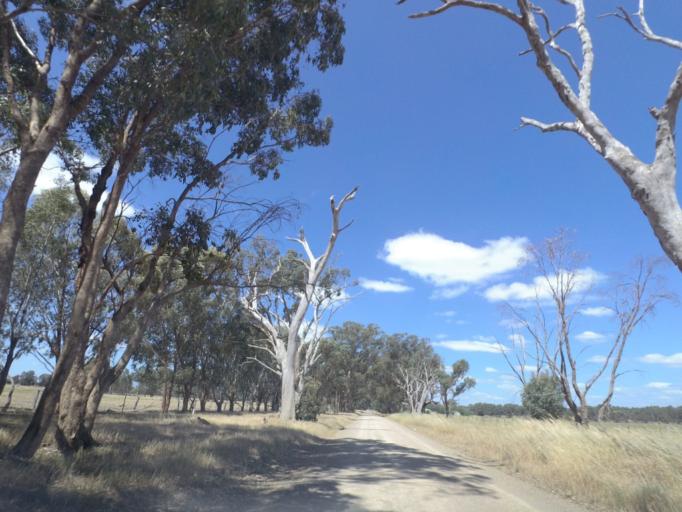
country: AU
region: Victoria
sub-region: Wangaratta
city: Wangaratta
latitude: -36.3999
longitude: 146.2924
